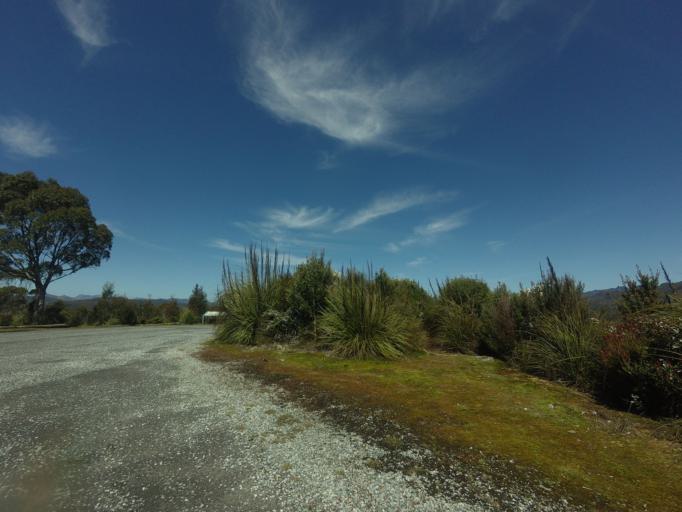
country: AU
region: Tasmania
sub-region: West Coast
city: Queenstown
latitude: -42.7833
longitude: 146.0322
